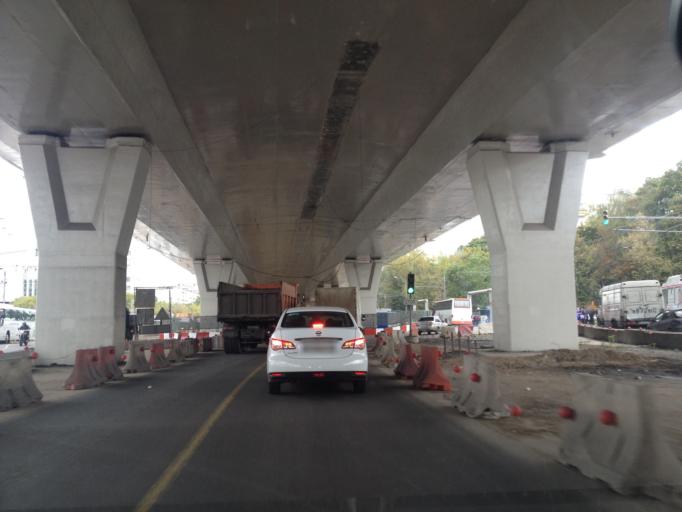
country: RU
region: Moscow
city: Metrogorodok
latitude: 55.8102
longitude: 37.7991
